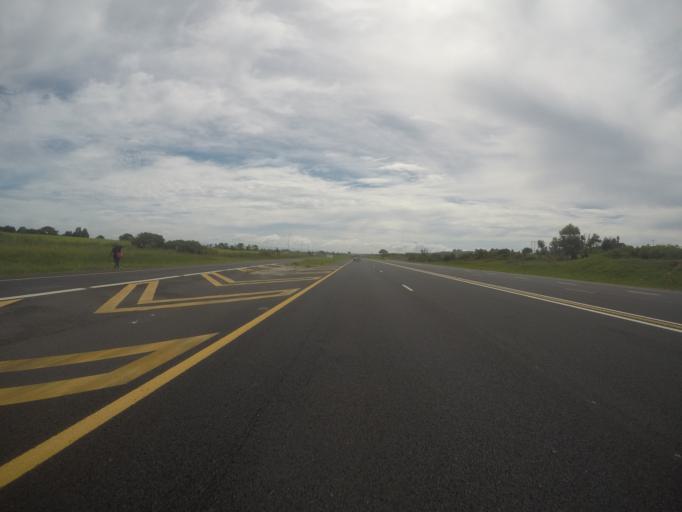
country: ZA
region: KwaZulu-Natal
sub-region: iLembe District Municipality
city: Mandeni
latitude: -29.0826
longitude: 31.6110
